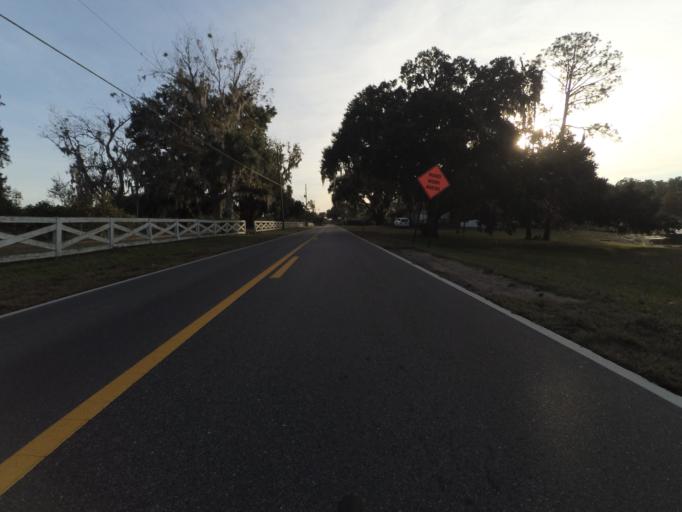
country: US
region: Florida
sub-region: Lake County
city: Umatilla
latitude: 28.9311
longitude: -81.6775
